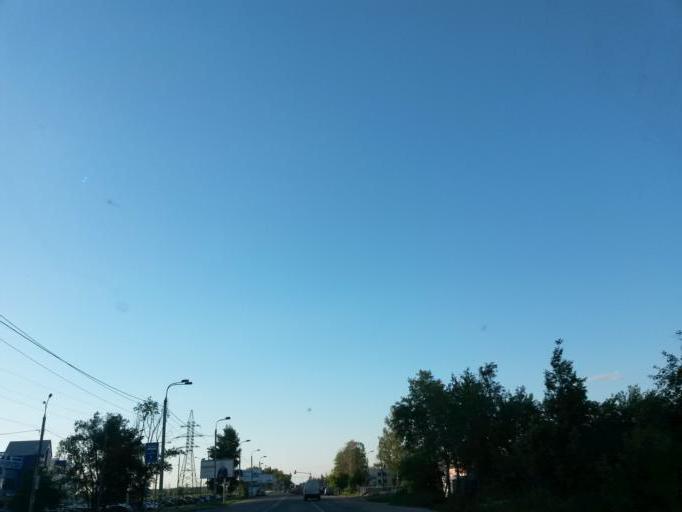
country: RU
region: Moskovskaya
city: Serpukhov
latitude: 54.9401
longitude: 37.4066
